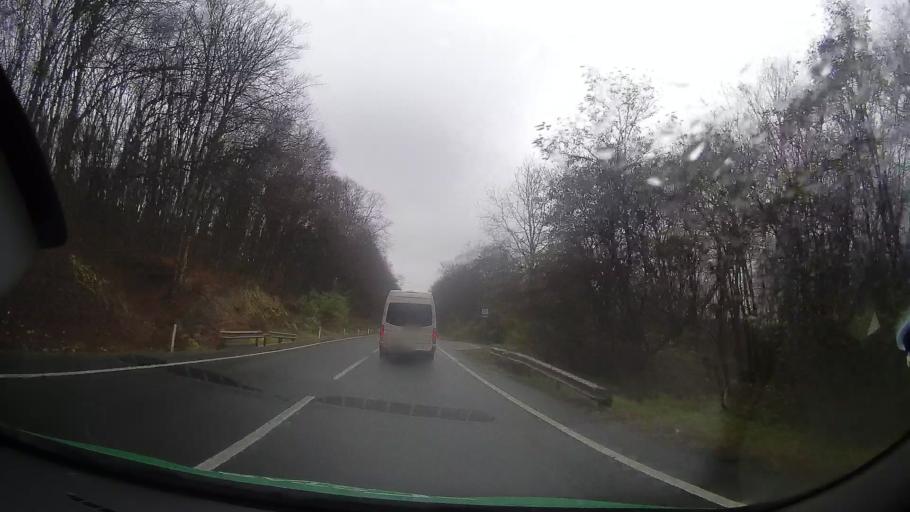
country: RO
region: Bistrita-Nasaud
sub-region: Comuna Galatii Bistritei
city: Galatii Bistritei
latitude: 47.0381
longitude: 24.4209
